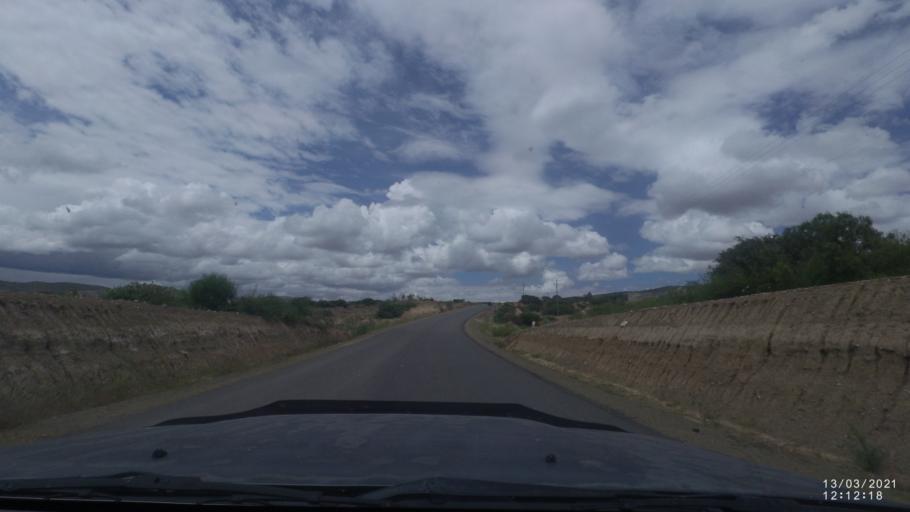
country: BO
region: Cochabamba
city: Tarata
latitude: -17.6689
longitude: -65.9626
